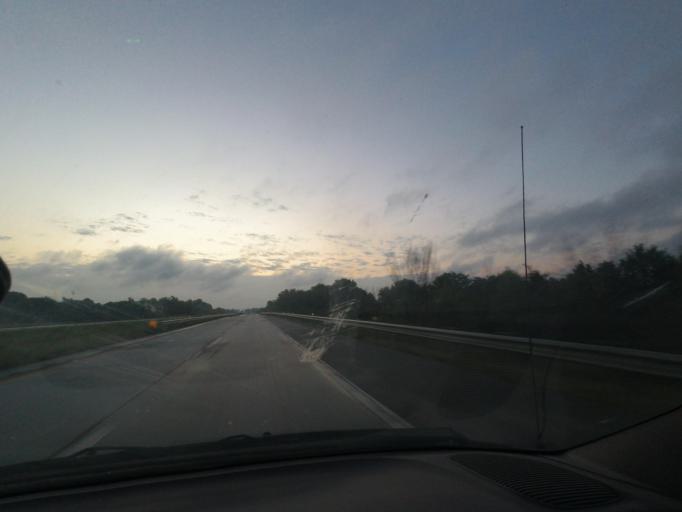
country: US
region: Missouri
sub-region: Linn County
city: Marceline
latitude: 39.7614
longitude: -92.9788
